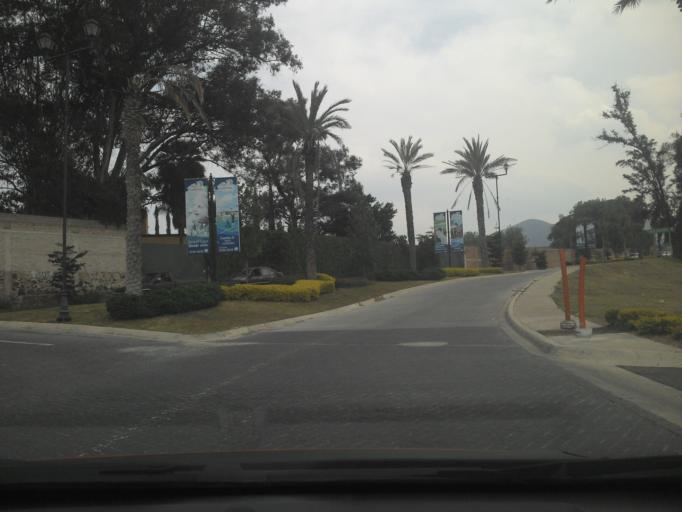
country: MX
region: Jalisco
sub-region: Tlajomulco de Zuniga
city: Lomas de San Agustin
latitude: 20.5314
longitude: -103.4753
